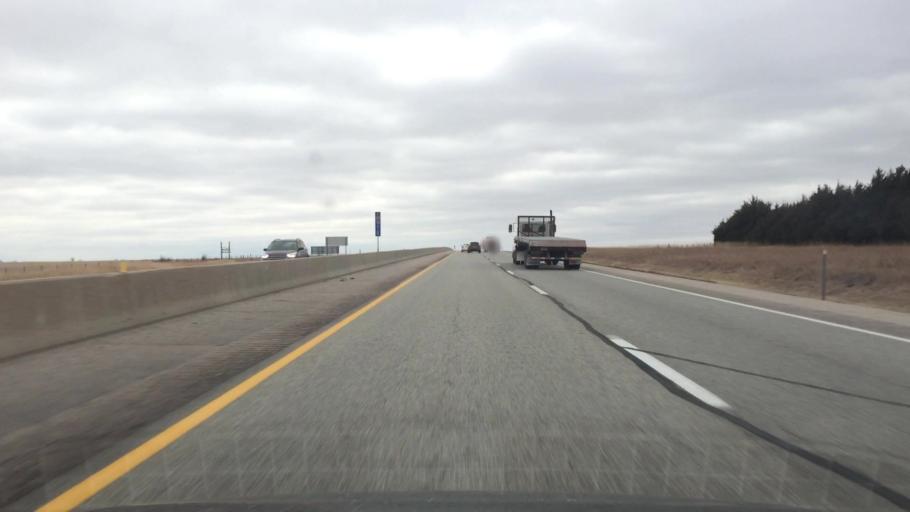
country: US
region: Kansas
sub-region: Butler County
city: El Dorado
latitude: 38.0424
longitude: -96.6458
